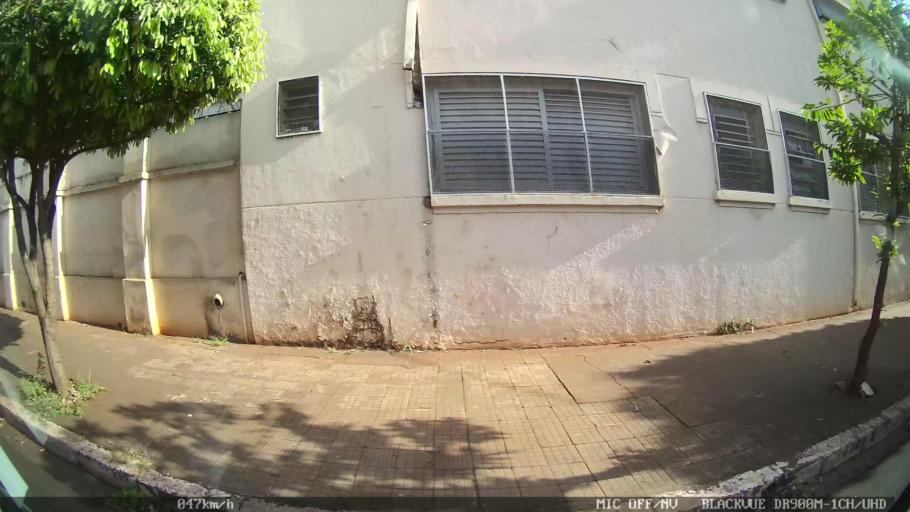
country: BR
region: Sao Paulo
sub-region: Ribeirao Preto
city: Ribeirao Preto
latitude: -21.1671
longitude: -47.8053
